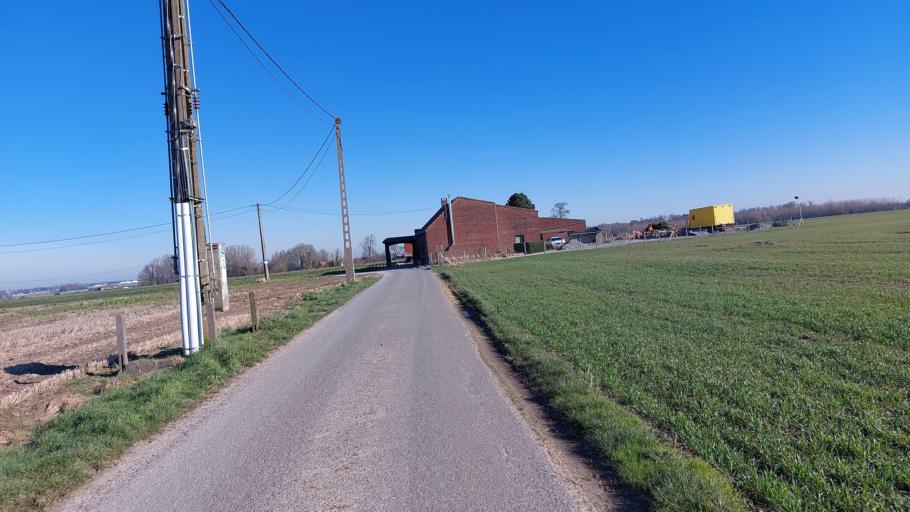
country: BE
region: Wallonia
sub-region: Province du Hainaut
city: Chievres
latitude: 50.5527
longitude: 3.8271
